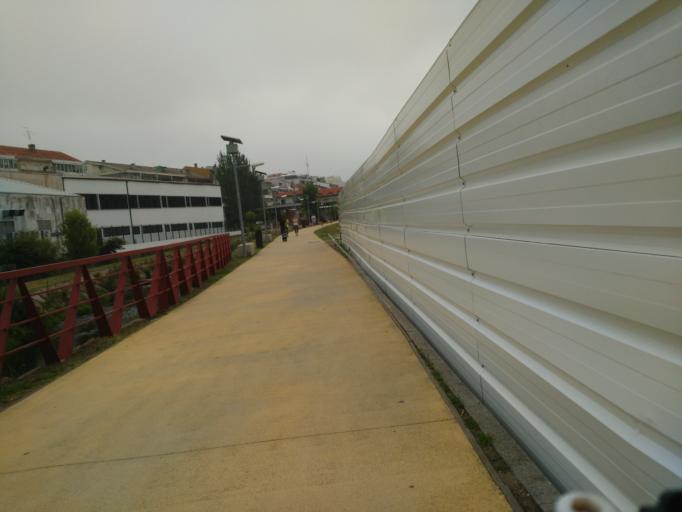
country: PT
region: Braga
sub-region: Braga
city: Braga
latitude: 41.5419
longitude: -8.4226
